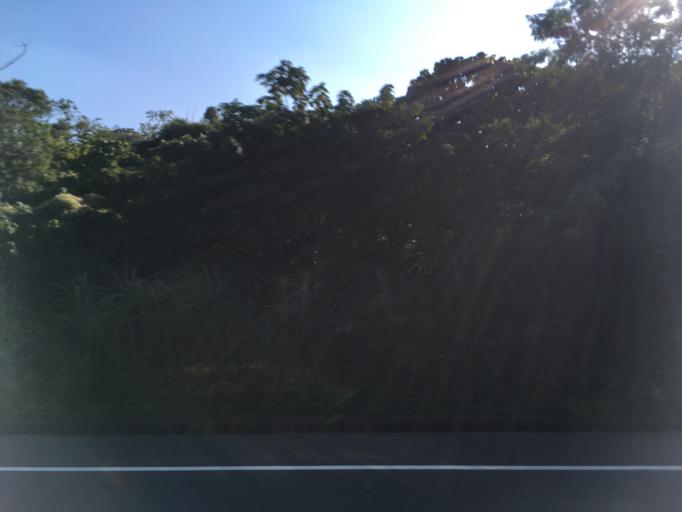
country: TW
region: Taiwan
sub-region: Chiayi
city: Jiayi Shi
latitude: 23.4452
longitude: 120.5021
